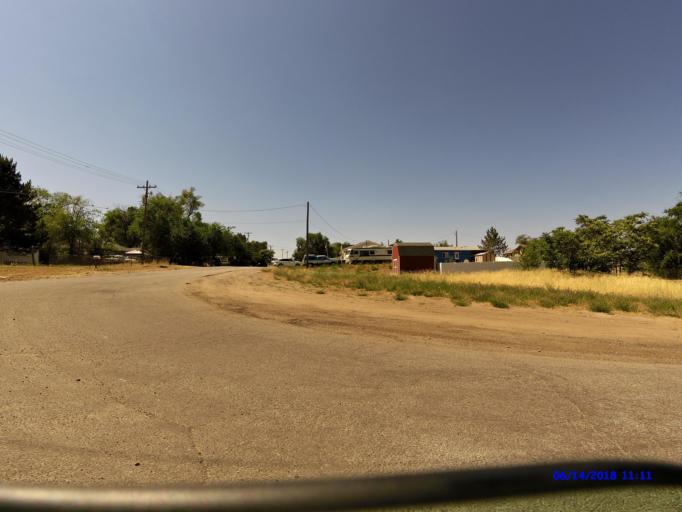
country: US
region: Utah
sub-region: Weber County
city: Ogden
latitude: 41.2194
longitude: -112.0010
